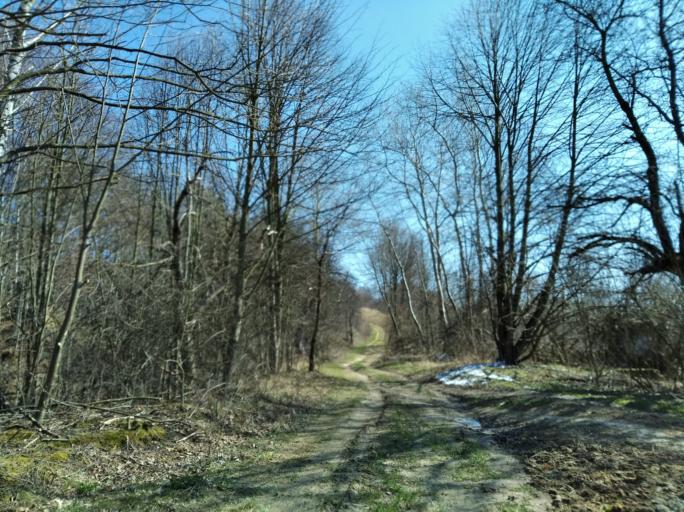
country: PL
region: Subcarpathian Voivodeship
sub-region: Powiat strzyzowski
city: Strzyzow
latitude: 49.8521
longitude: 21.8184
